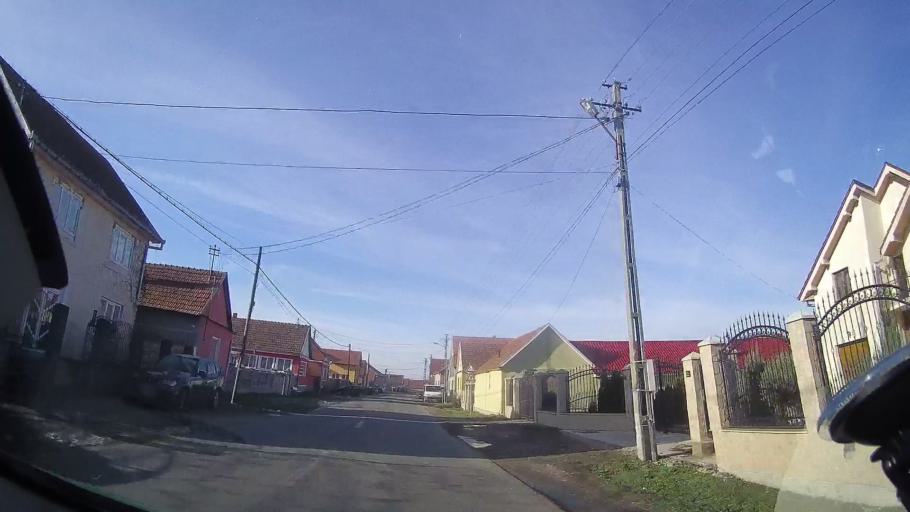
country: RO
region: Bihor
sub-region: Comuna Astileu
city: Astileu
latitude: 47.0294
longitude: 22.3898
